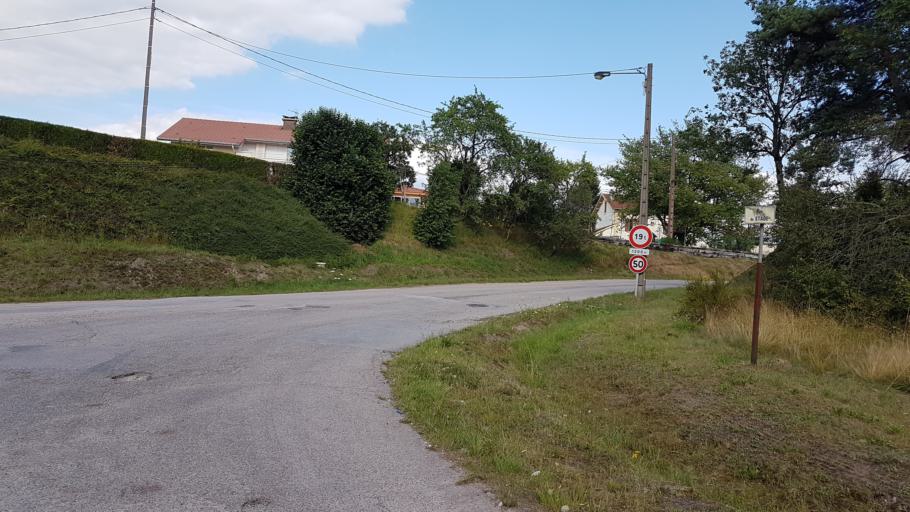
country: FR
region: Lorraine
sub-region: Departement des Vosges
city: Pouxeux
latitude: 48.1073
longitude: 6.5757
